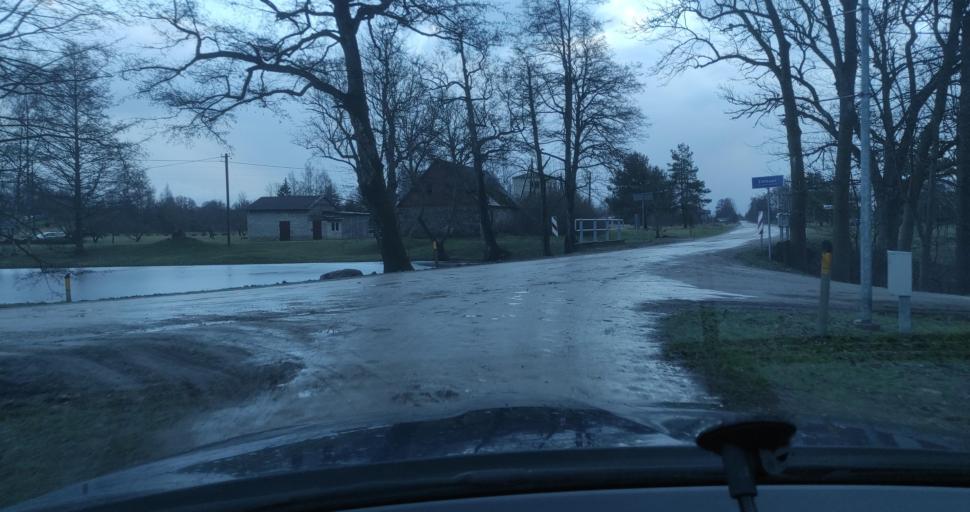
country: LV
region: Pavilostas
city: Pavilosta
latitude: 56.7485
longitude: 21.0770
